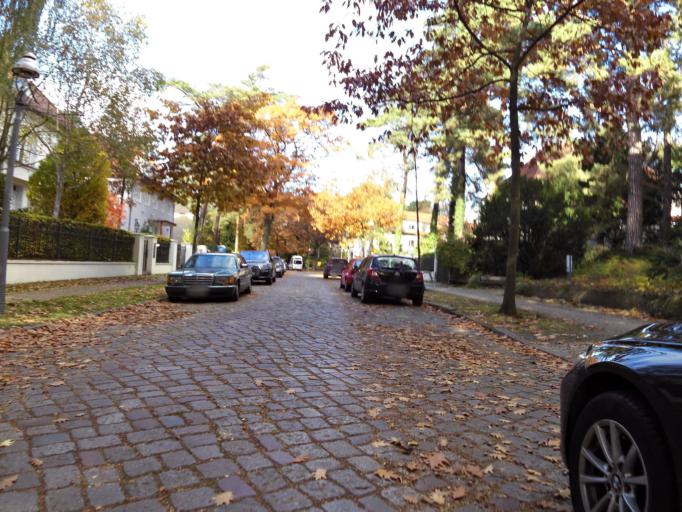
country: DE
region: Berlin
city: Zehlendorf Bezirk
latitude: 52.4411
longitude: 13.2307
